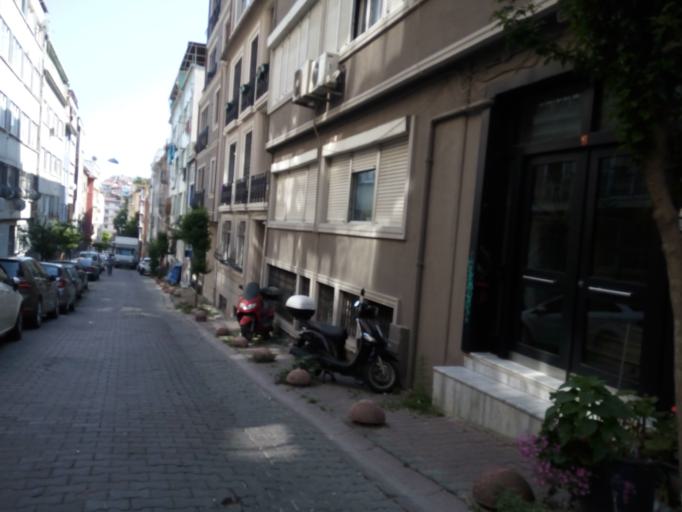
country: TR
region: Istanbul
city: Eminoenue
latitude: 41.0345
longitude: 28.9860
